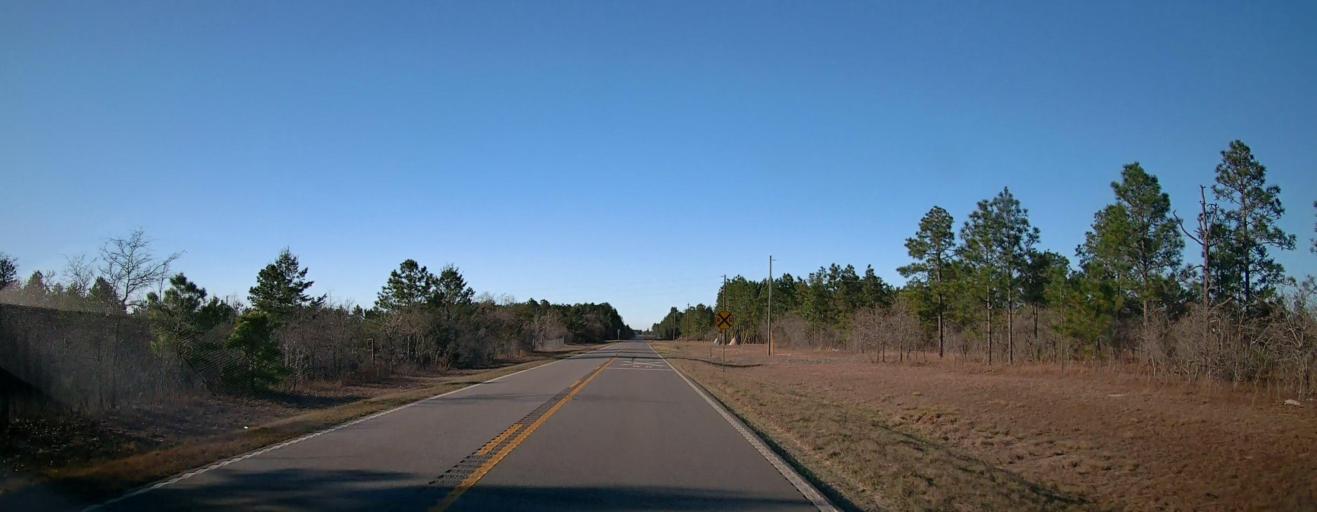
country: US
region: Georgia
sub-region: Talbot County
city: Talbotton
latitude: 32.5711
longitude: -84.4414
